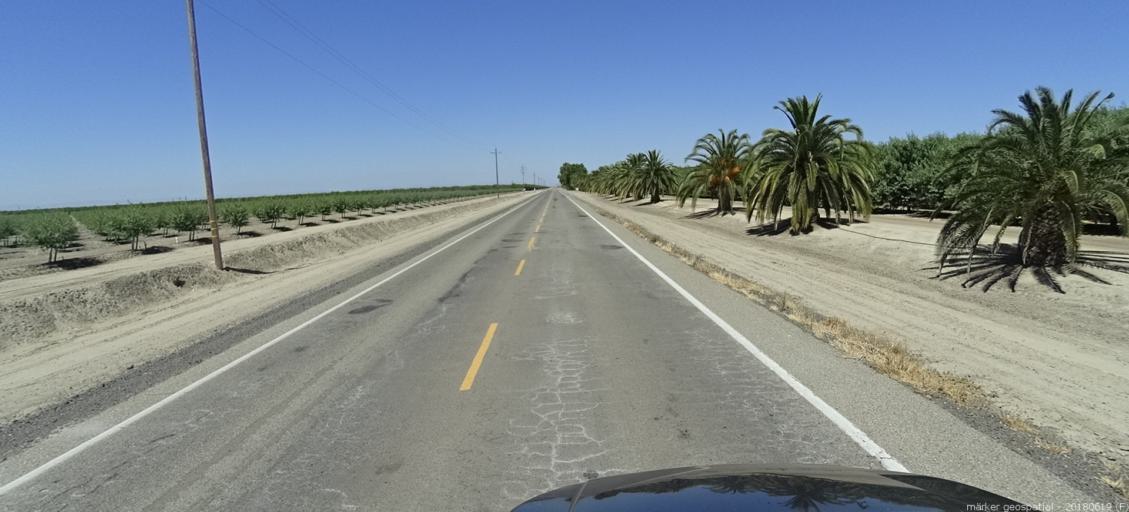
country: US
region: California
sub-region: Fresno County
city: Mendota
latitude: 36.8510
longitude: -120.2875
